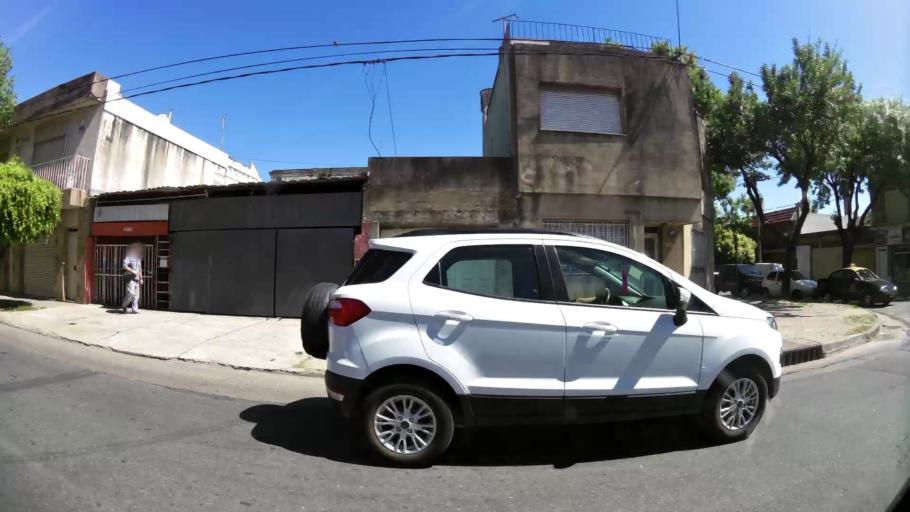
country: AR
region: Santa Fe
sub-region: Departamento de Rosario
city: Rosario
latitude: -32.9366
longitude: -60.6856
